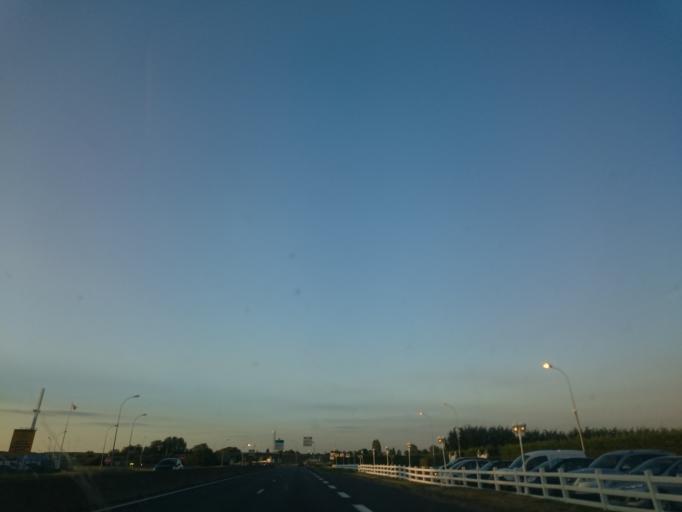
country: FR
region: Ile-de-France
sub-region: Departement de l'Essonne
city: Egly
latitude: 48.5699
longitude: 2.2333
